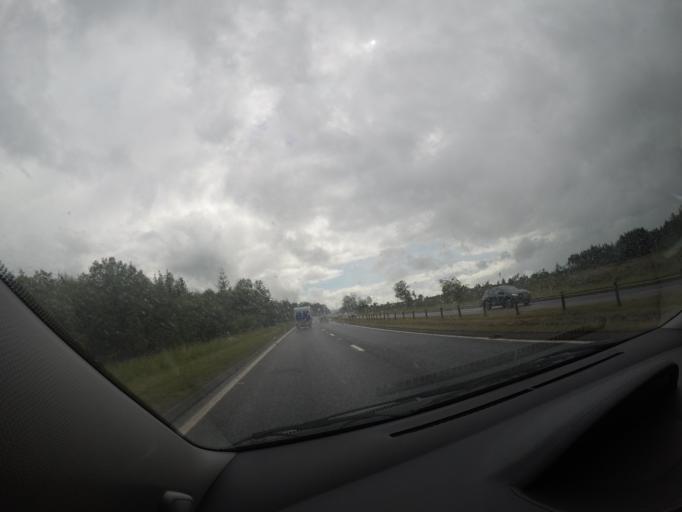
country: GB
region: Scotland
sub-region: Perth and Kinross
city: Methven
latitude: 56.3610
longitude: -3.5574
